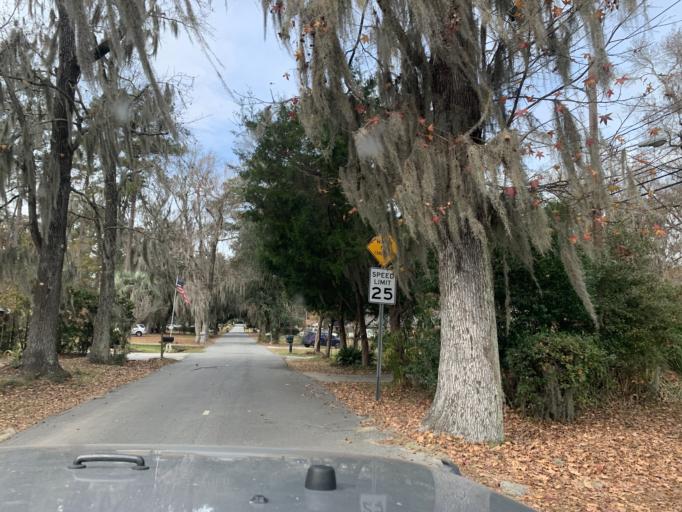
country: US
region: Georgia
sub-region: Chatham County
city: Montgomery
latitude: 31.9682
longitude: -81.1293
